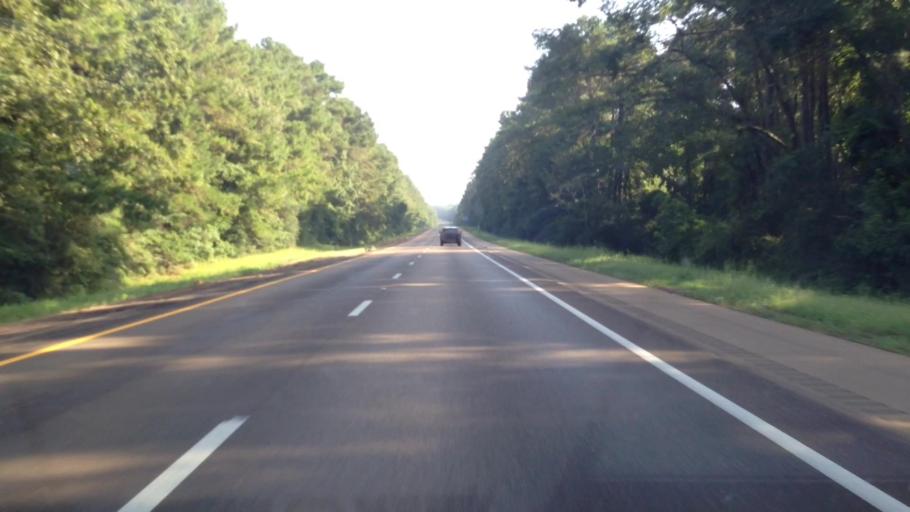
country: US
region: Mississippi
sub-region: Pike County
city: Summit
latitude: 31.3162
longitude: -90.4775
